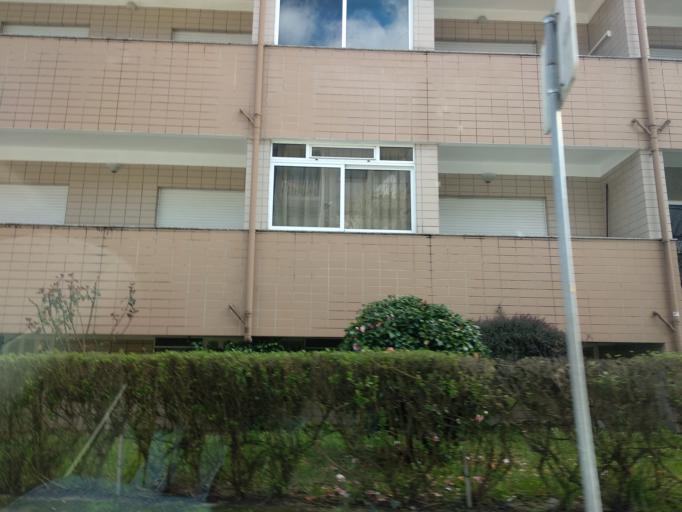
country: PT
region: Braga
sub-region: Braga
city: Braga
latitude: 41.5640
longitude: -8.4100
